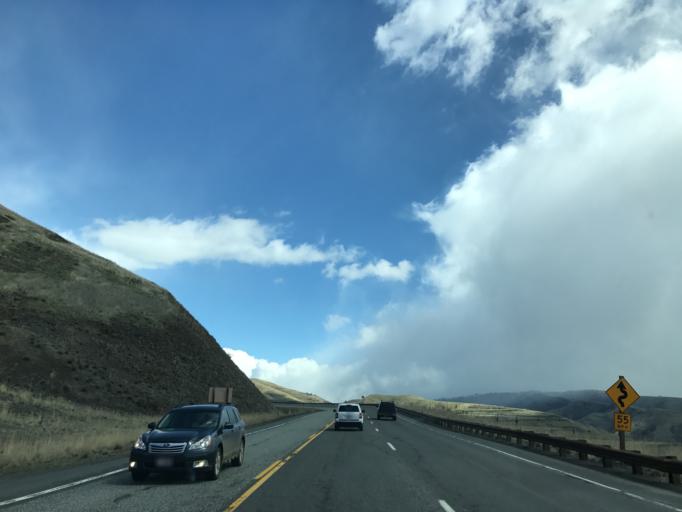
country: US
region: Idaho
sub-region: Idaho County
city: Grangeville
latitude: 45.8056
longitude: -116.2837
